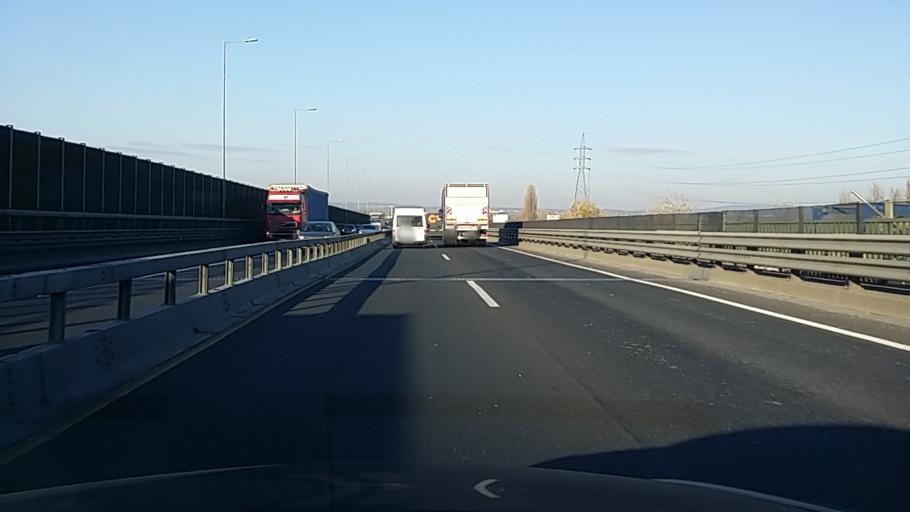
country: HU
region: Pest
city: Dunaharaszti
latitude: 47.3715
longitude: 19.0919
